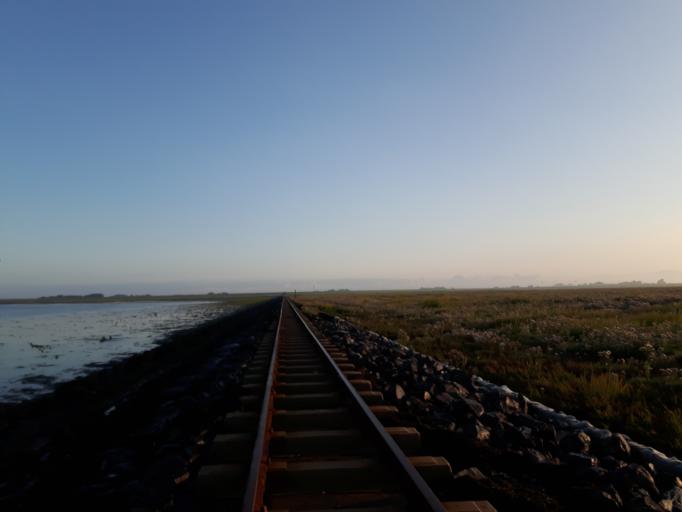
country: DE
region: Schleswig-Holstein
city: Dagebull
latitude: 54.7150
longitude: 8.7115
